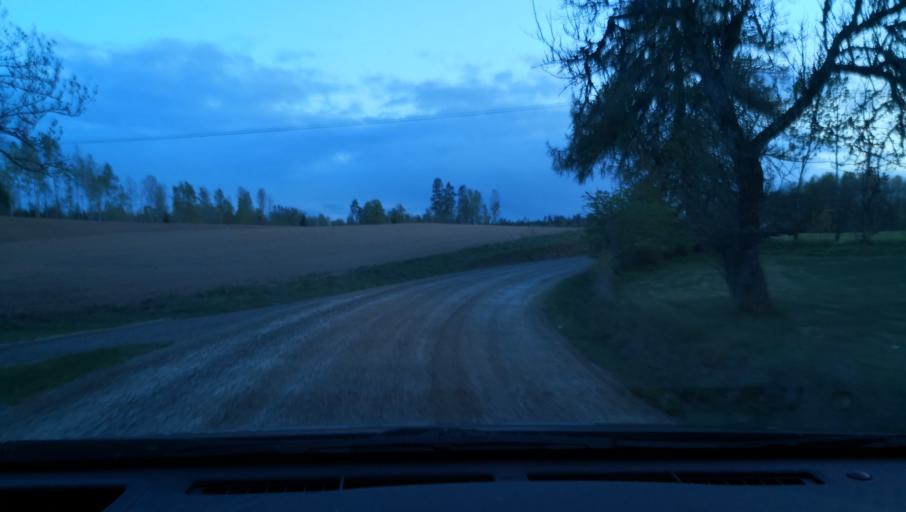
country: SE
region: OErebro
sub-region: Askersunds Kommun
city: Askersund
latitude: 58.9956
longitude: 14.9007
